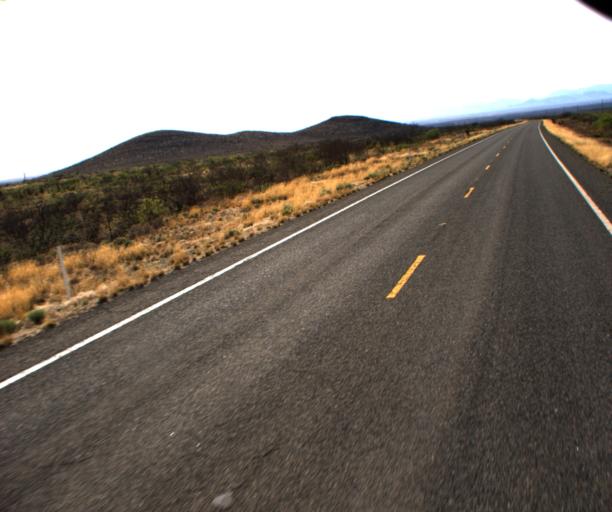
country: US
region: Arizona
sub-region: Cochise County
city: Willcox
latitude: 32.1850
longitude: -109.6730
